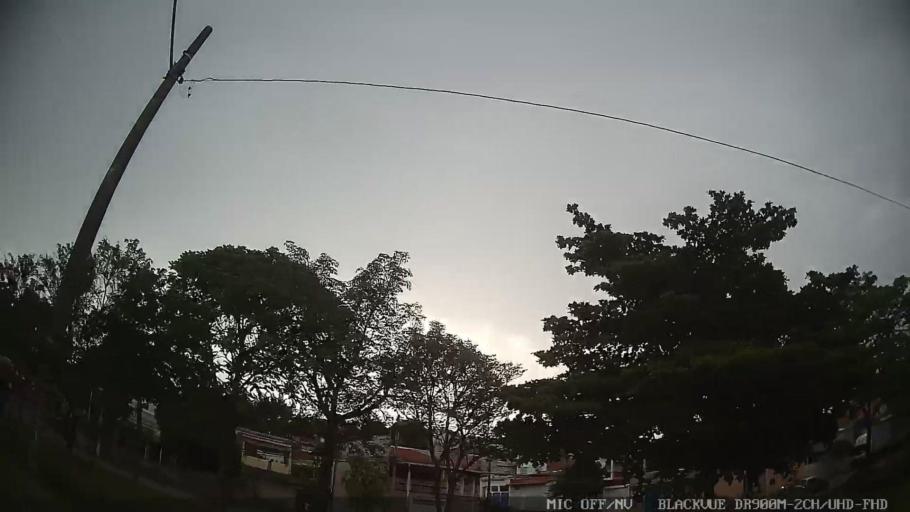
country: BR
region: Sao Paulo
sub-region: Pedreira
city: Pedreira
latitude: -22.7173
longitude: -46.8930
